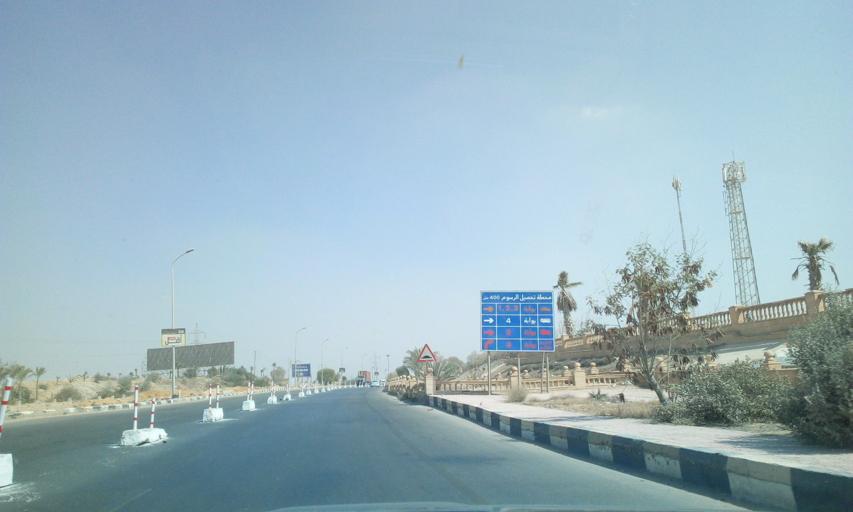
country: EG
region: Muhafazat al Qahirah
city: Halwan
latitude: 29.9657
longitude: 31.4745
